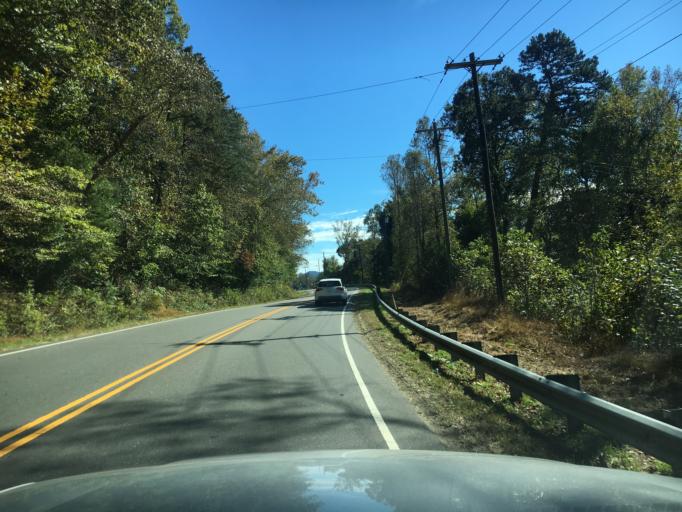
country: US
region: North Carolina
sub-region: Burke County
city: Morganton
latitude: 35.7392
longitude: -81.7107
